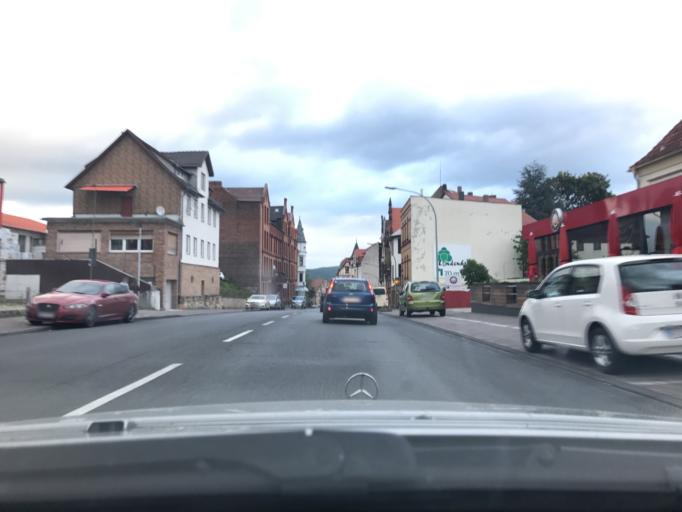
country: DE
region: Hesse
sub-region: Regierungsbezirk Kassel
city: Eschwege
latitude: 51.1868
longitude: 10.0491
